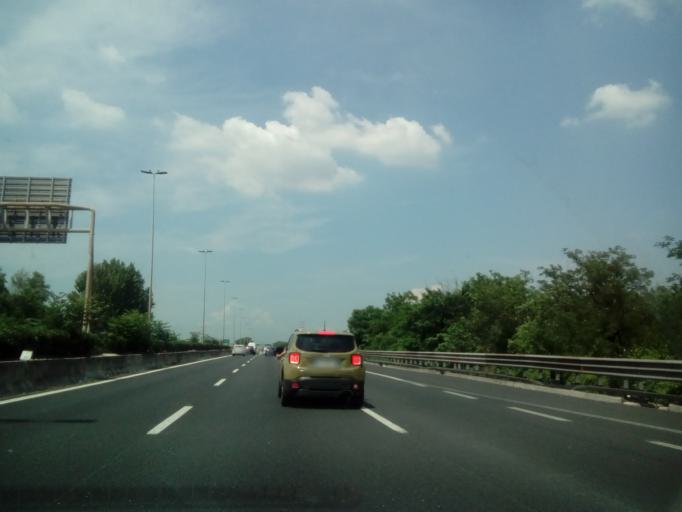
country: IT
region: Latium
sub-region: Citta metropolitana di Roma Capitale
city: Setteville
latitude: 41.8980
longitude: 12.6154
